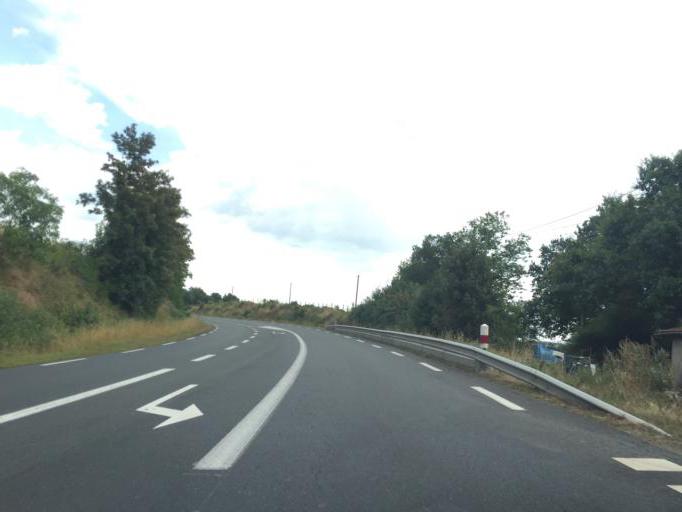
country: FR
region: Rhone-Alpes
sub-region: Departement de la Loire
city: Saint-Symphorien-de-Lay
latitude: 45.9531
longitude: 4.1924
